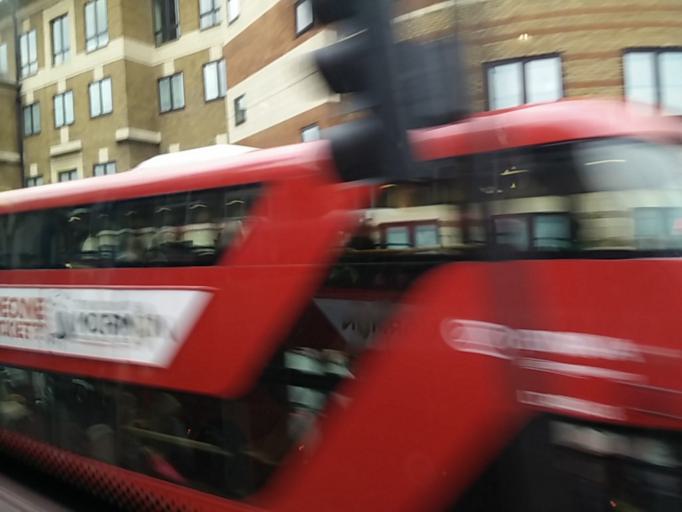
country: GB
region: England
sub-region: Greater London
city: Islington
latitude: 51.5321
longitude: -0.1063
